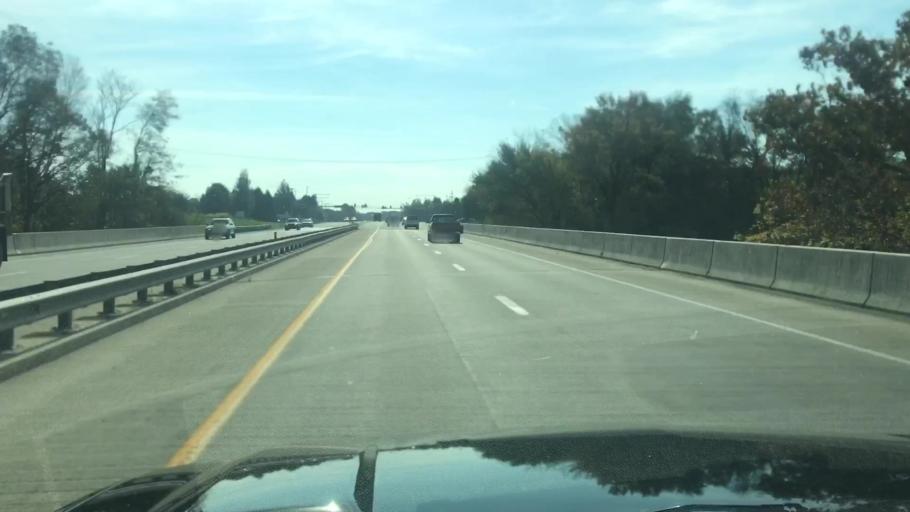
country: US
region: Pennsylvania
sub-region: Cumberland County
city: Mechanicsburg
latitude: 40.2545
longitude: -77.0317
